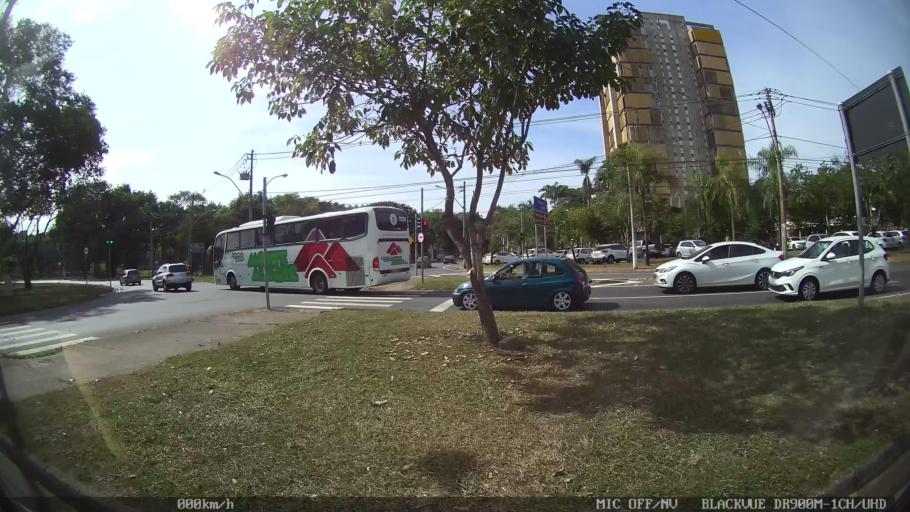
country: BR
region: Sao Paulo
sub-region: Piracicaba
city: Piracicaba
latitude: -22.7286
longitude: -47.6655
